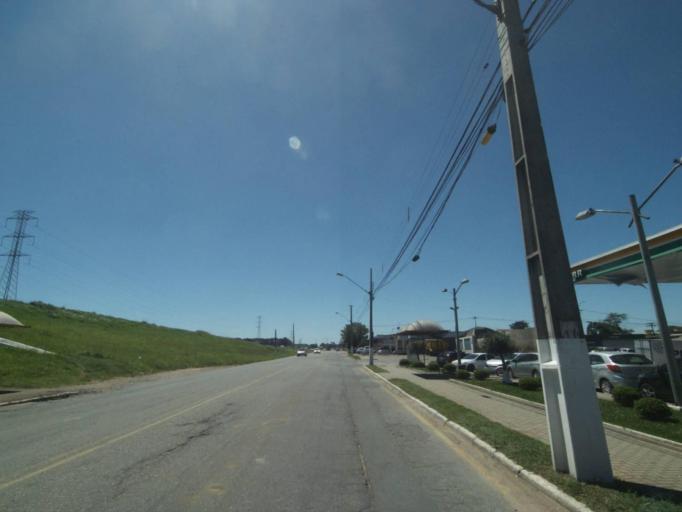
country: BR
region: Parana
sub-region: Curitiba
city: Curitiba
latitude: -25.4828
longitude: -49.3478
